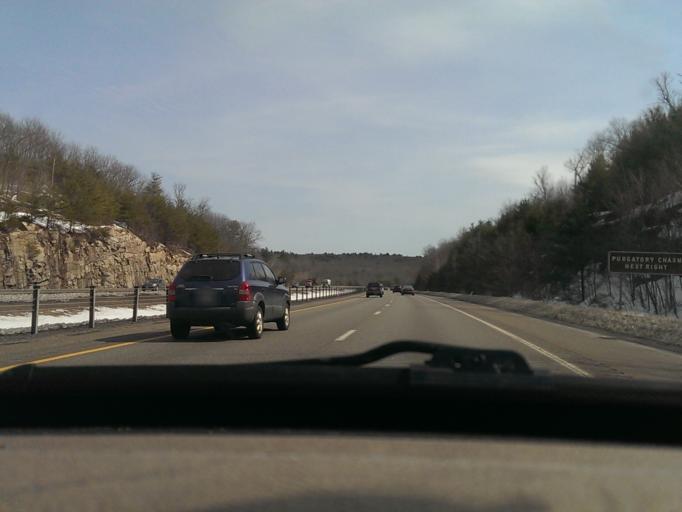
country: US
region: Massachusetts
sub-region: Worcester County
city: Whitinsville
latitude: 42.1391
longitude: -71.7100
